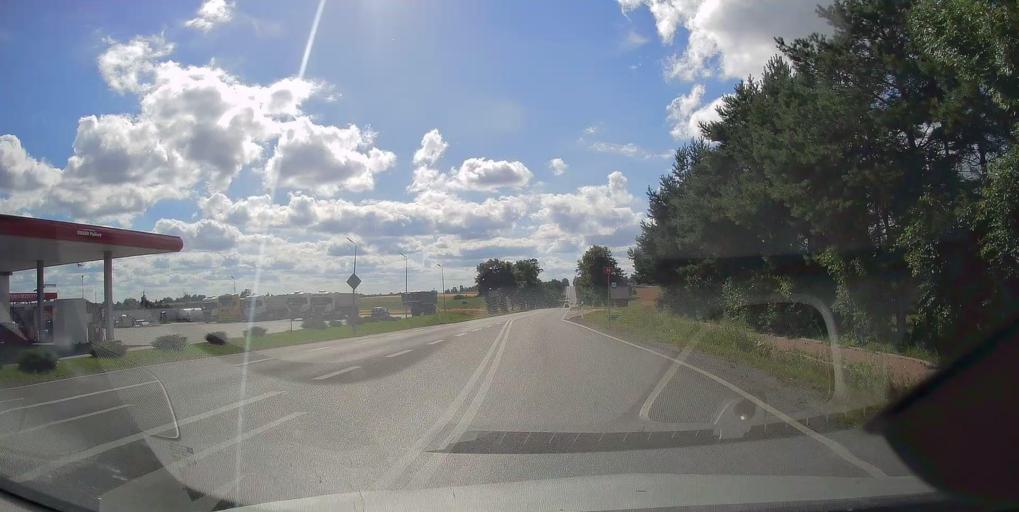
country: PL
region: Swietokrzyskie
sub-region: Powiat opatowski
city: Backowice
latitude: 50.7990
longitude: 21.2324
